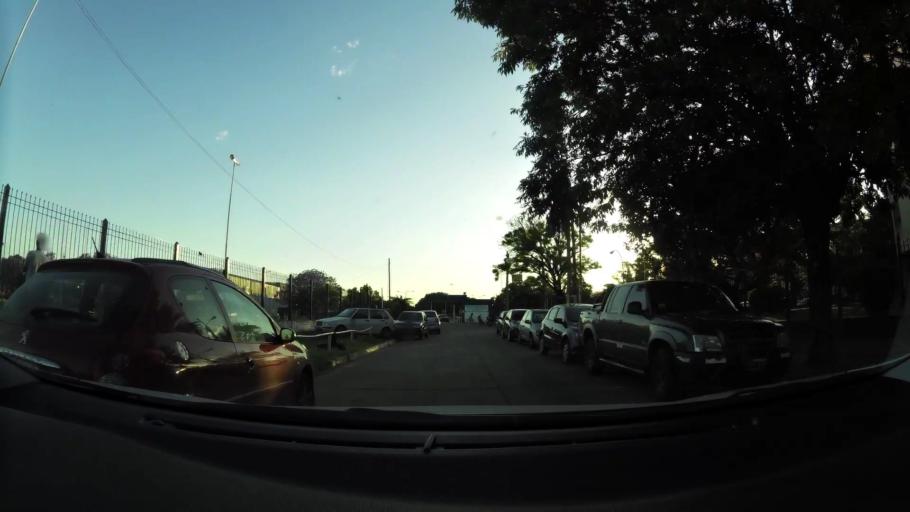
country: AR
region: Buenos Aires F.D.
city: Villa Lugano
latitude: -34.6976
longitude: -58.4770
